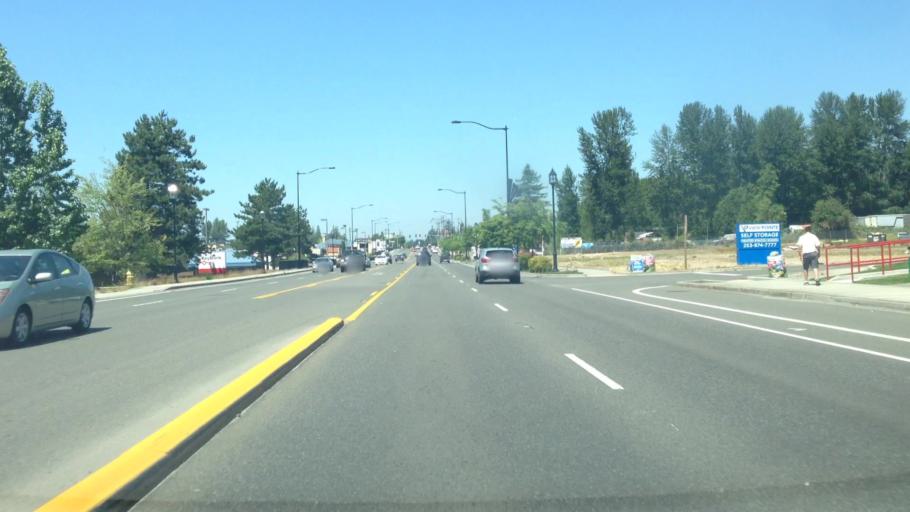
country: US
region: Washington
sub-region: Pierce County
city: Edgewood
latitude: 47.2457
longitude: -122.2938
